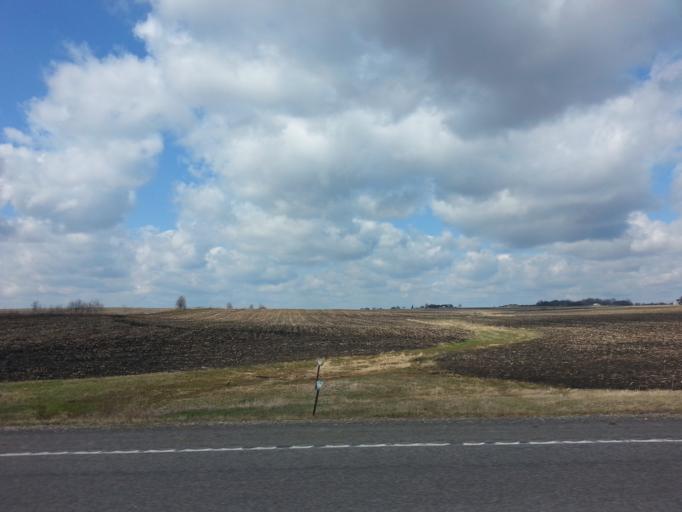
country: US
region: Minnesota
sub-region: Dodge County
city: Mantorville
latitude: 44.0798
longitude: -92.7026
